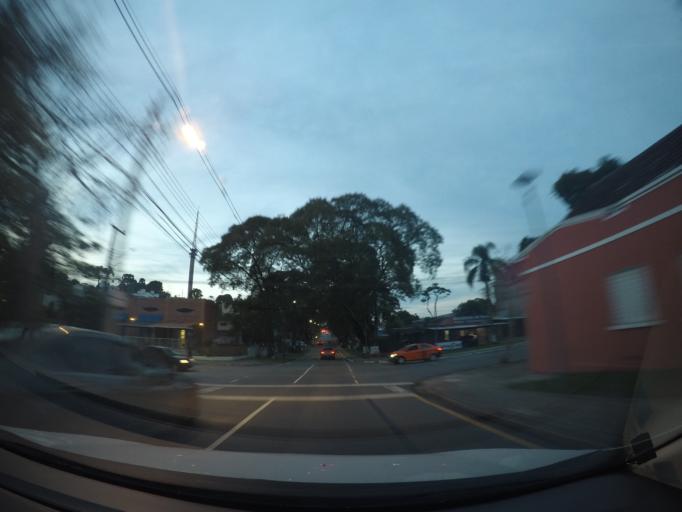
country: BR
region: Parana
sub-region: Curitiba
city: Curitiba
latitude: -25.4196
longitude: -49.2869
